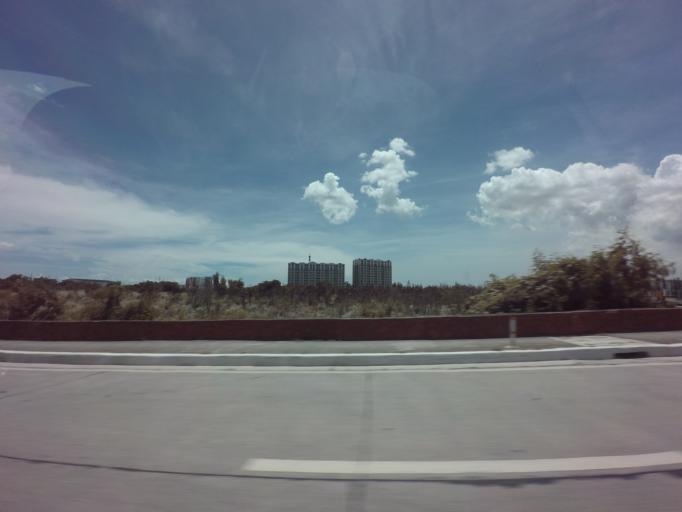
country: PH
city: Sambayanihan People's Village
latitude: 14.4868
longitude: 120.9980
